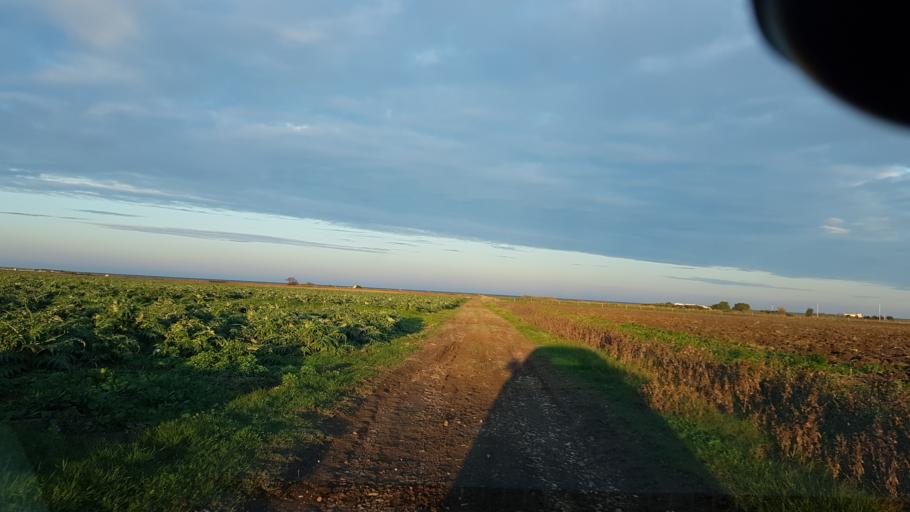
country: IT
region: Apulia
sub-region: Provincia di Brindisi
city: La Rosa
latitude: 40.6082
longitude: 18.0113
